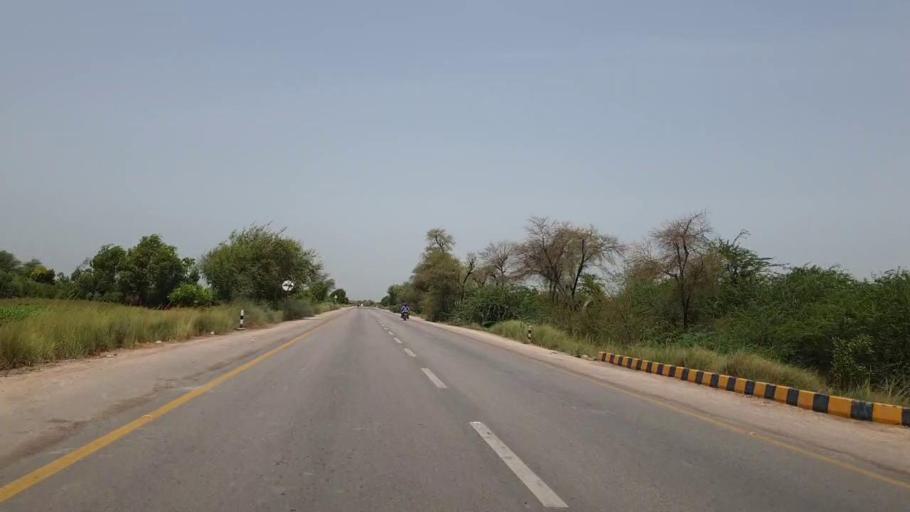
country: PK
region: Sindh
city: Nawabshah
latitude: 26.2133
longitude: 68.5126
